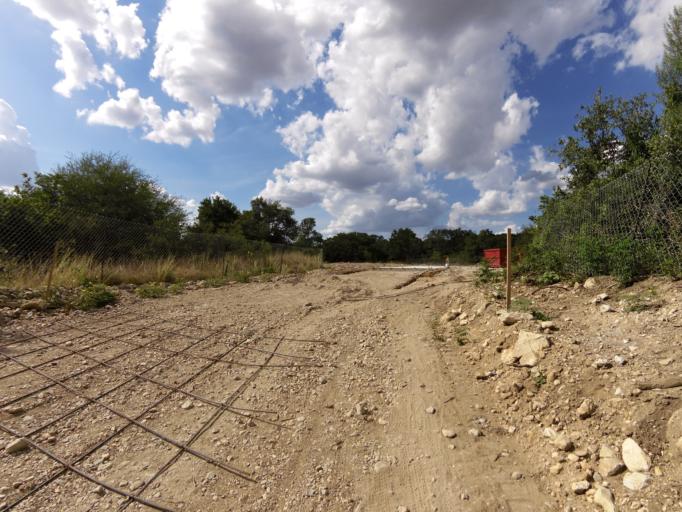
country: US
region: Texas
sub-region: Bexar County
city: Shavano Park
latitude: 29.5957
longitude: -98.5960
